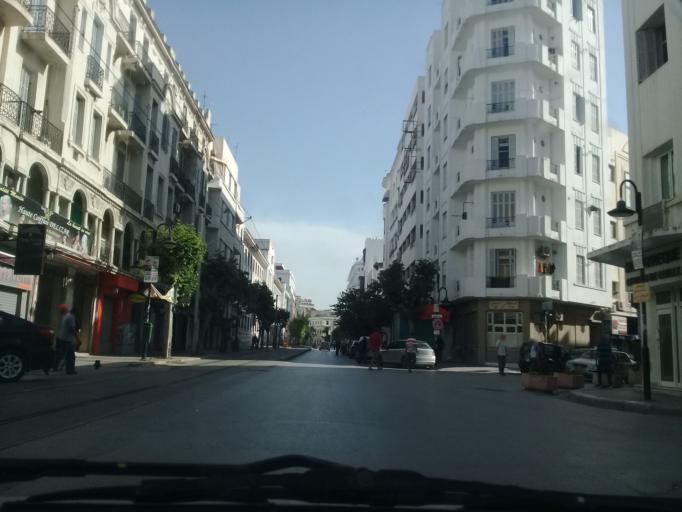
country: TN
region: Tunis
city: Tunis
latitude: 36.8035
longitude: 10.1794
